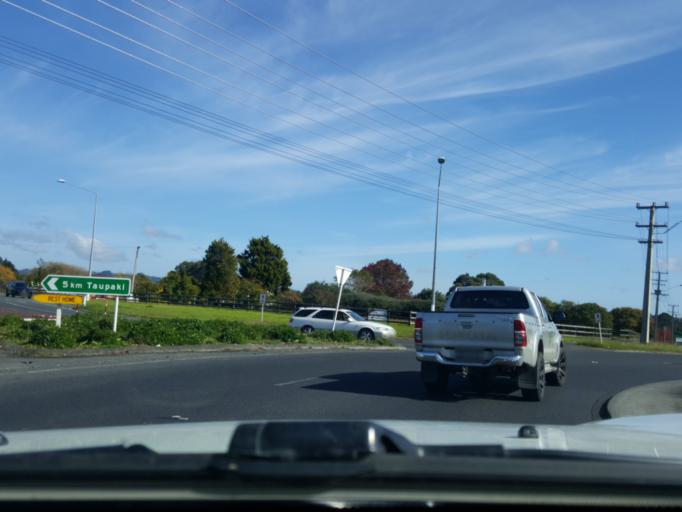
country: NZ
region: Auckland
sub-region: Auckland
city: Rosebank
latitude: -36.7875
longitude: 174.5771
